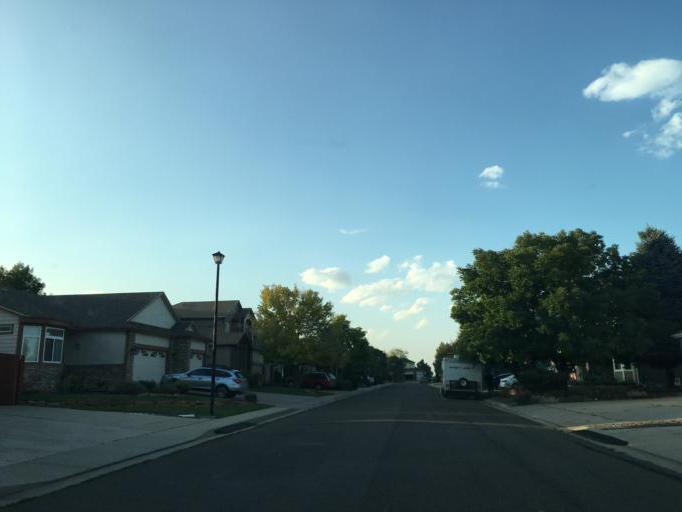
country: US
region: Colorado
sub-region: Jefferson County
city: Applewood
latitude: 39.7922
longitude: -105.1445
